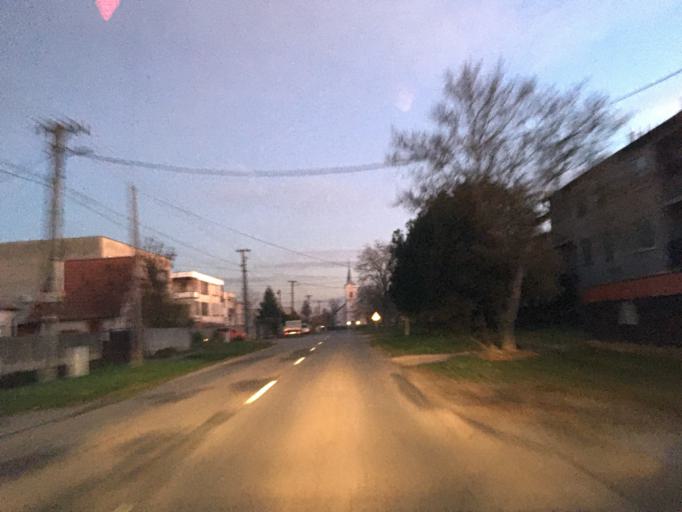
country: SK
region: Nitriansky
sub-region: Okres Komarno
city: Hurbanovo
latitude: 47.9016
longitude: 18.1392
